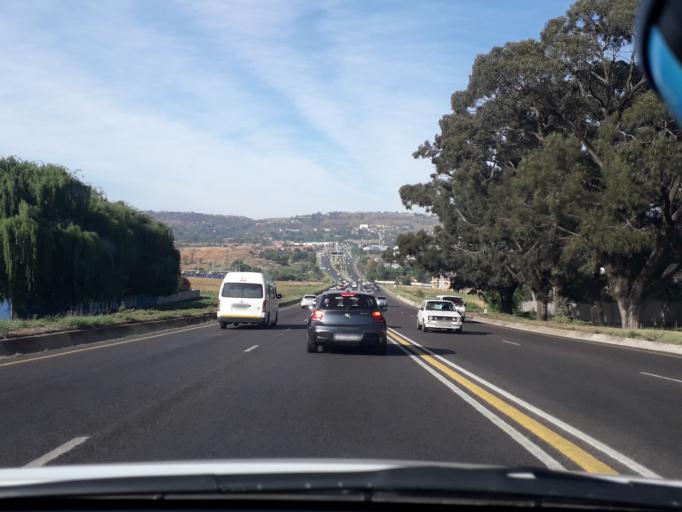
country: ZA
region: Gauteng
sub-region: City of Johannesburg Metropolitan Municipality
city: Roodepoort
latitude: -26.1181
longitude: 27.9149
